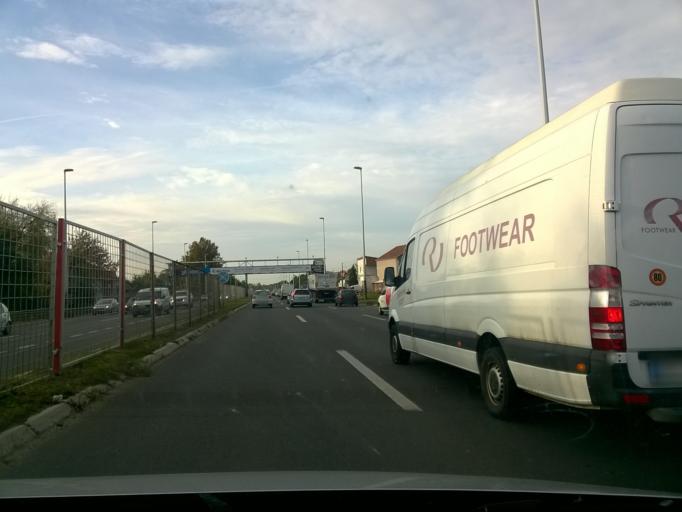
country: RS
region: Central Serbia
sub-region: Belgrade
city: Zemun
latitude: 44.8445
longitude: 20.3698
